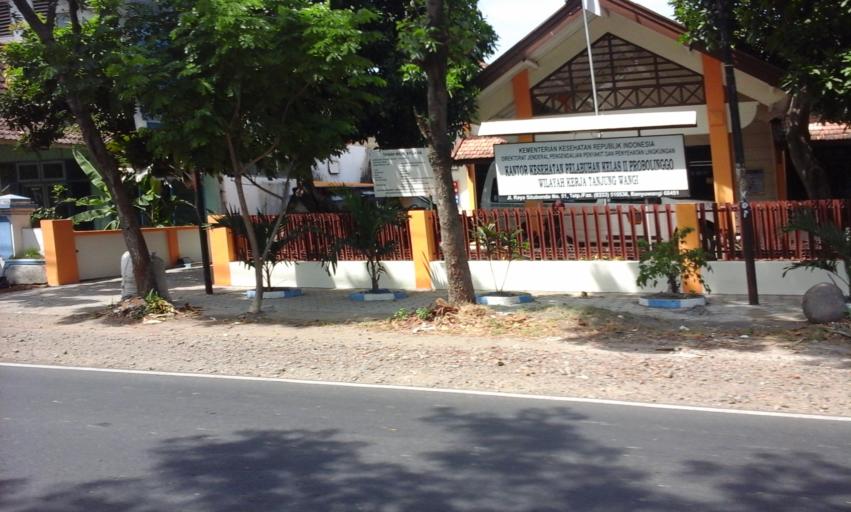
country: ID
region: East Java
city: Klatakan
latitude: -8.1293
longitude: 114.3983
